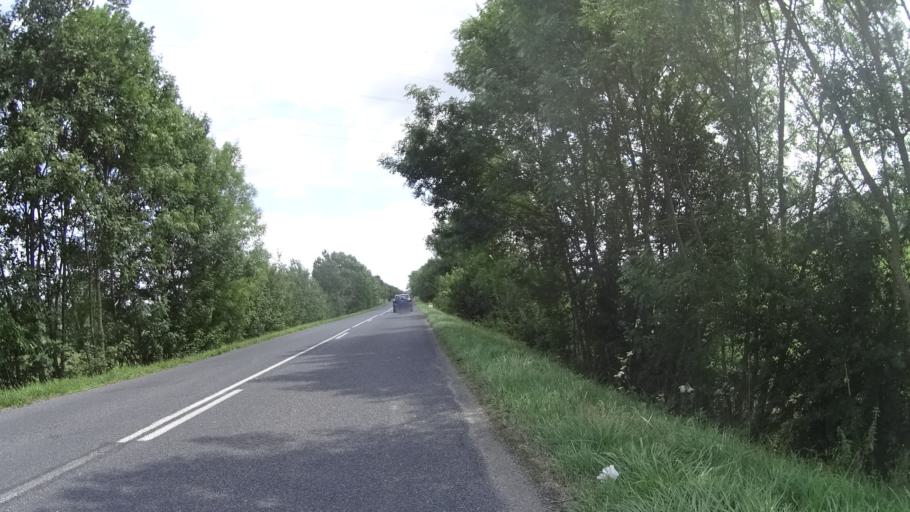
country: FR
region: Lorraine
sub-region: Departement de la Meuse
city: Vignot
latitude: 48.7576
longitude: 5.6084
